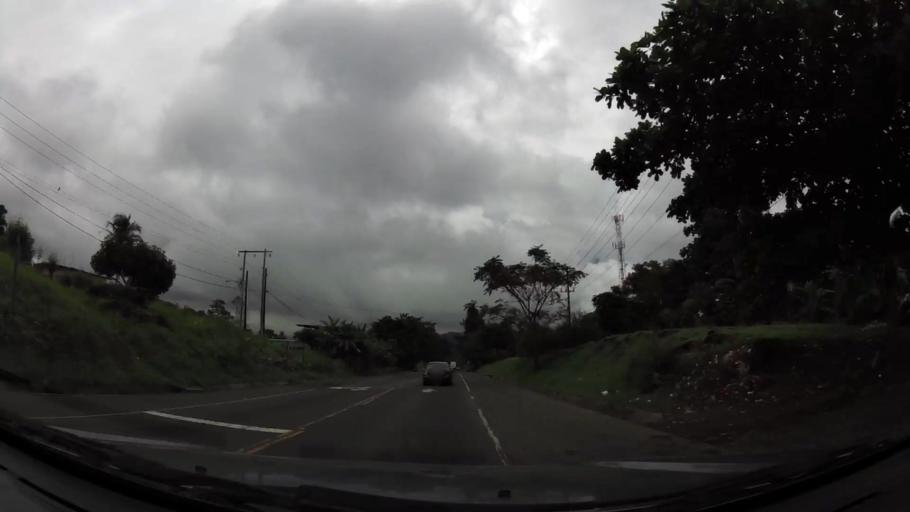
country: PA
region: Panama
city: Chilibre
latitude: 9.1956
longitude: -79.6210
